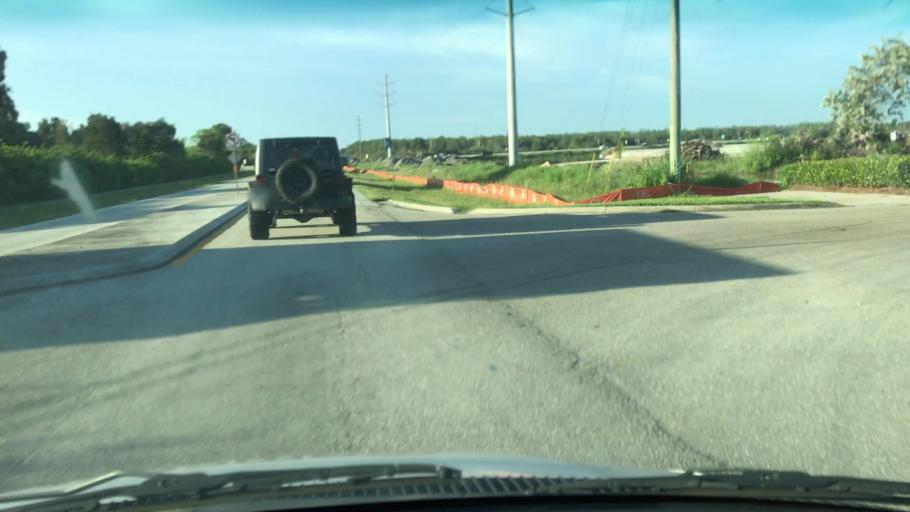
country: US
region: Florida
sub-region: Lee County
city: Villas
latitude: 26.5322
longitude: -81.8468
